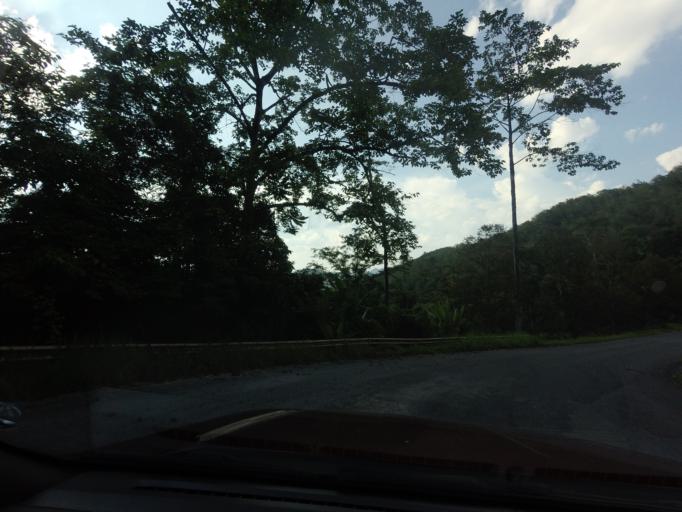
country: TH
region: Yala
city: Than To
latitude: 6.1462
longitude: 101.2828
